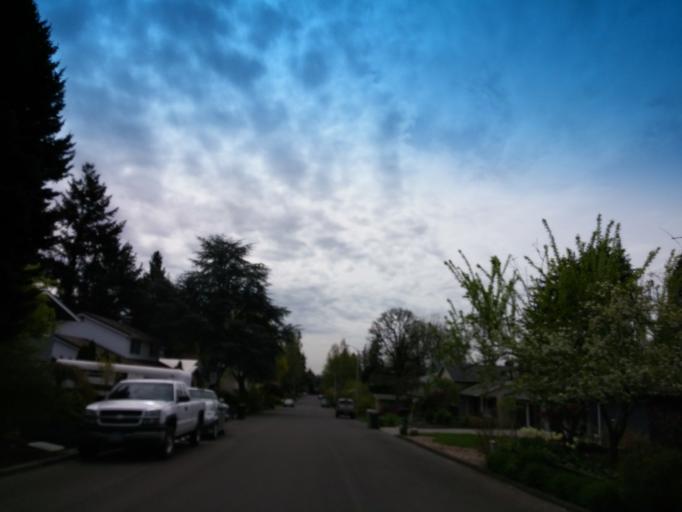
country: US
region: Oregon
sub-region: Washington County
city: Cedar Mill
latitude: 45.5321
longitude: -122.8109
